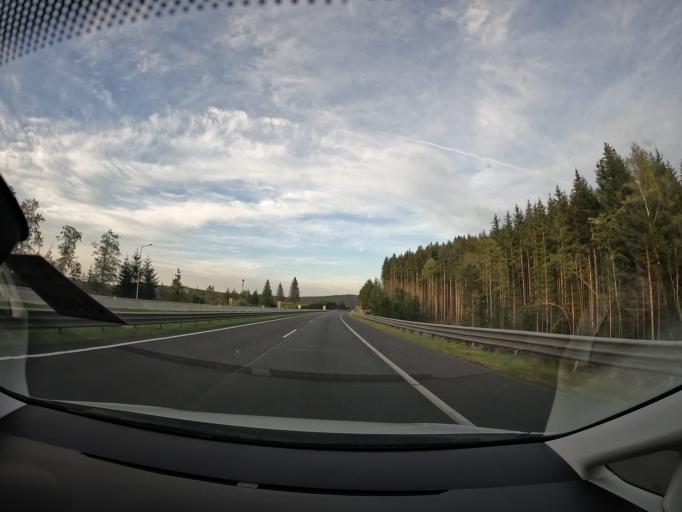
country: AT
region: Styria
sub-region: Politischer Bezirk Voitsberg
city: Modriach
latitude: 46.9556
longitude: 15.0133
